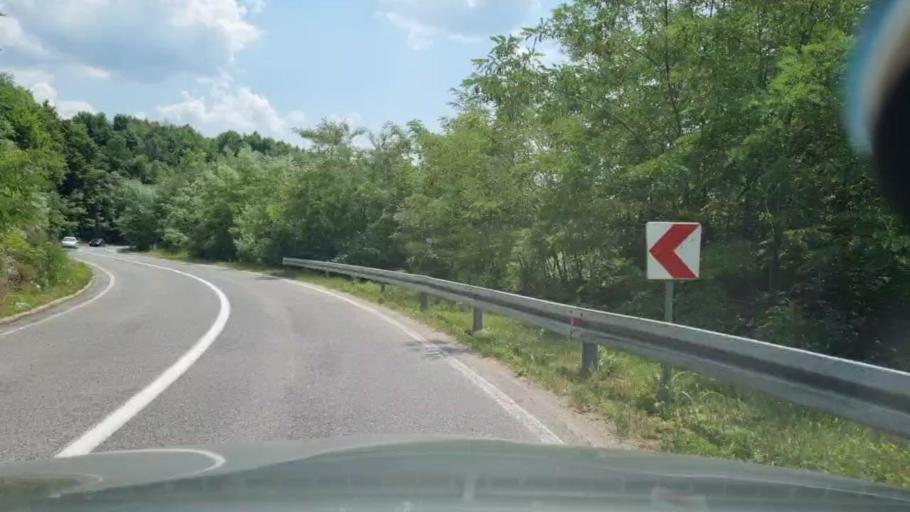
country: BA
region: Federation of Bosnia and Herzegovina
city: Tojsici
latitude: 44.5389
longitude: 18.8497
